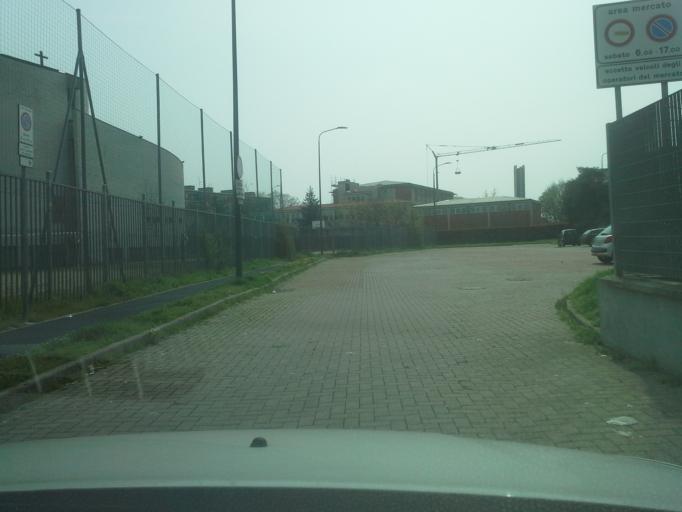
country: IT
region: Lombardy
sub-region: Citta metropolitana di Milano
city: Cesano Boscone
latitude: 45.4537
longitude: 9.0803
